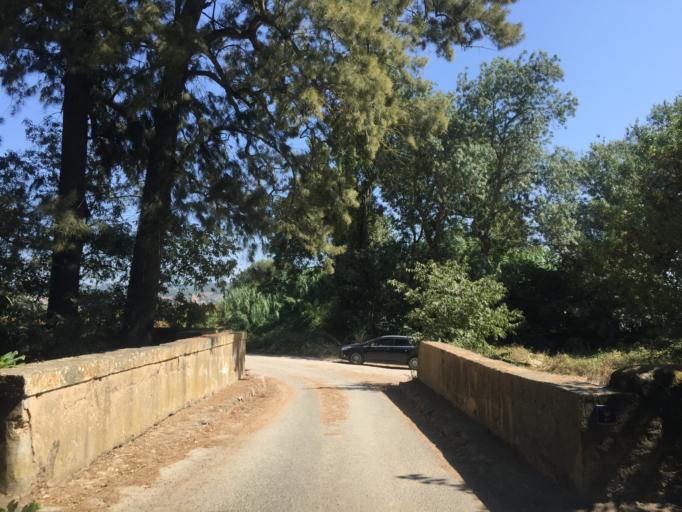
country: PT
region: Santarem
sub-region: Chamusca
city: Vila Nova da Barquinha
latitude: 39.4454
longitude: -8.4490
